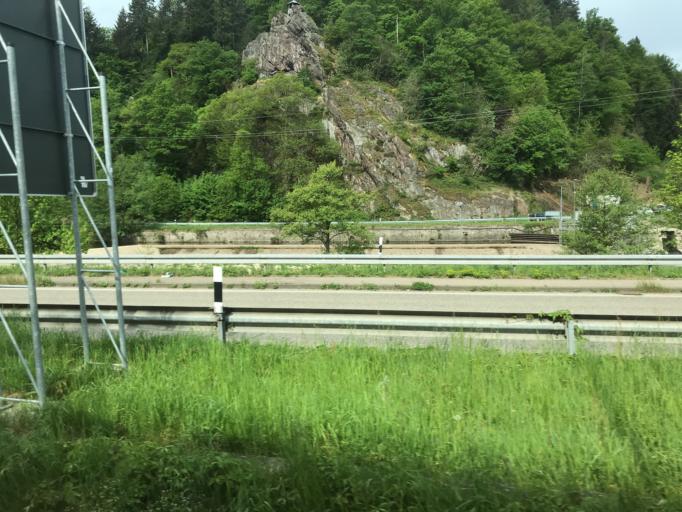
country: DE
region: Baden-Wuerttemberg
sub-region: Karlsruhe Region
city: Gernsbach
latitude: 48.7487
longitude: 8.3488
